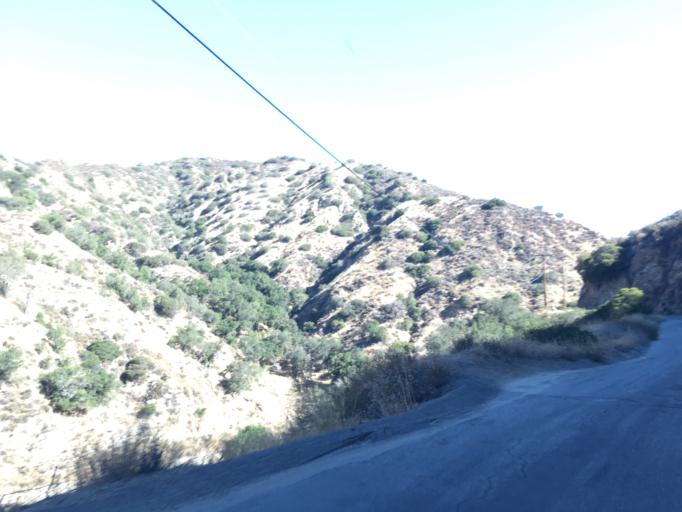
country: US
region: California
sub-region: Los Angeles County
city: La Verne
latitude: 34.1568
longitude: -117.7722
